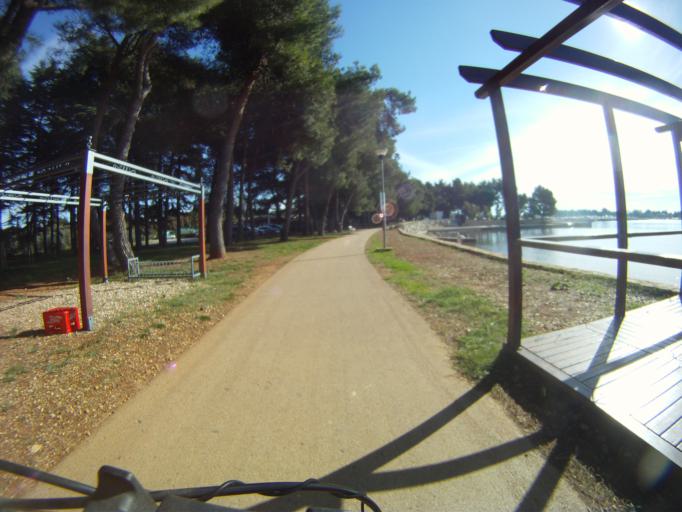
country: HR
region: Istarska
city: Novigrad
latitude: 45.3241
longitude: 13.5590
